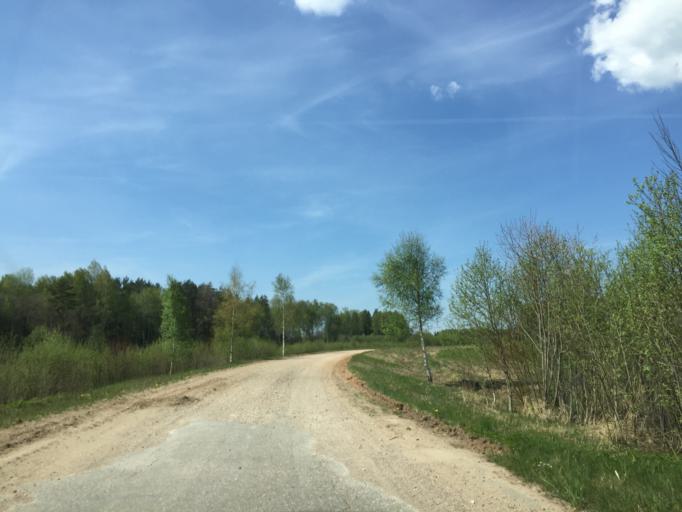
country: LV
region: Limbazu Rajons
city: Limbazi
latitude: 57.3848
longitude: 24.5842
